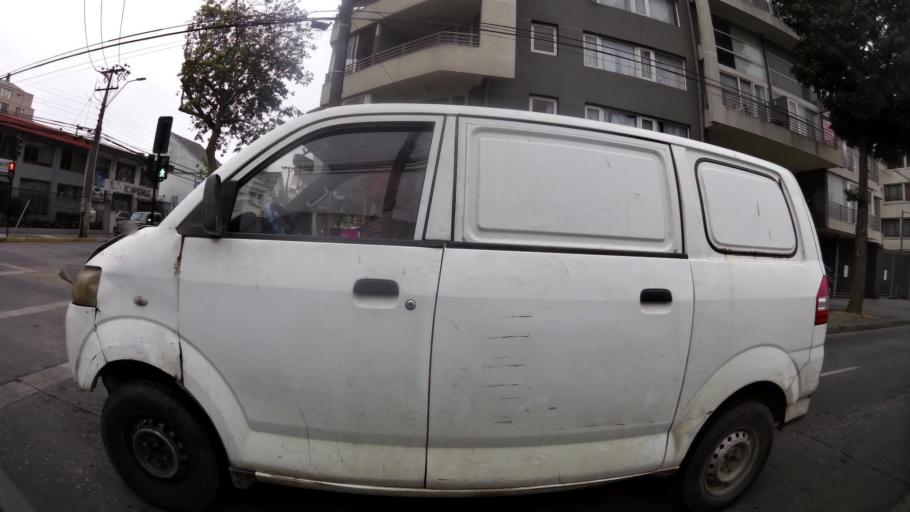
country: CL
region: Biobio
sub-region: Provincia de Concepcion
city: Concepcion
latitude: -36.8323
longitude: -73.0523
